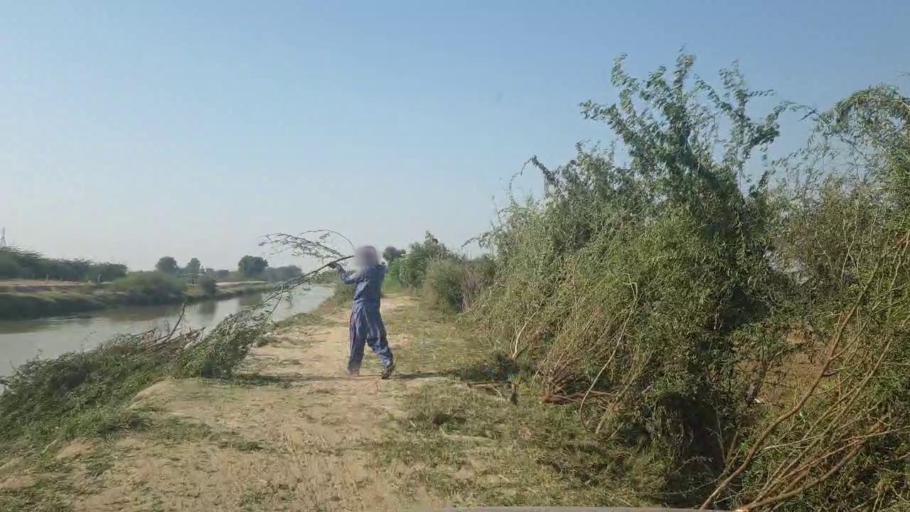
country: PK
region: Sindh
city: Badin
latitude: 24.6792
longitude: 68.8558
